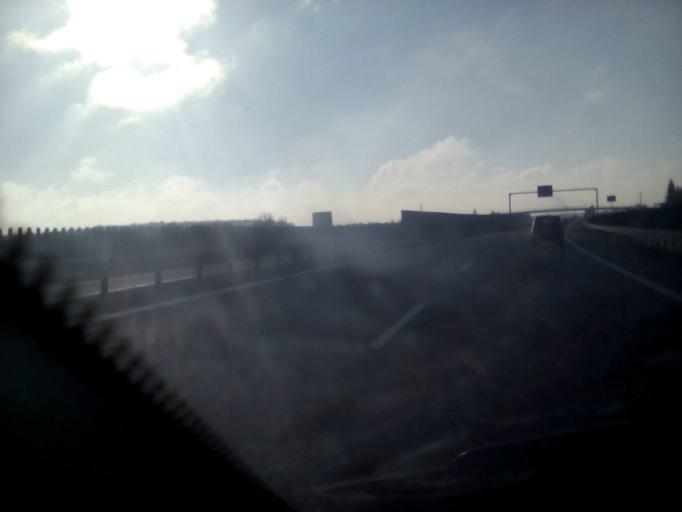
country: PL
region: Masovian Voivodeship
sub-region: Powiat grojecki
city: Grojec
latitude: 51.8437
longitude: 20.8740
